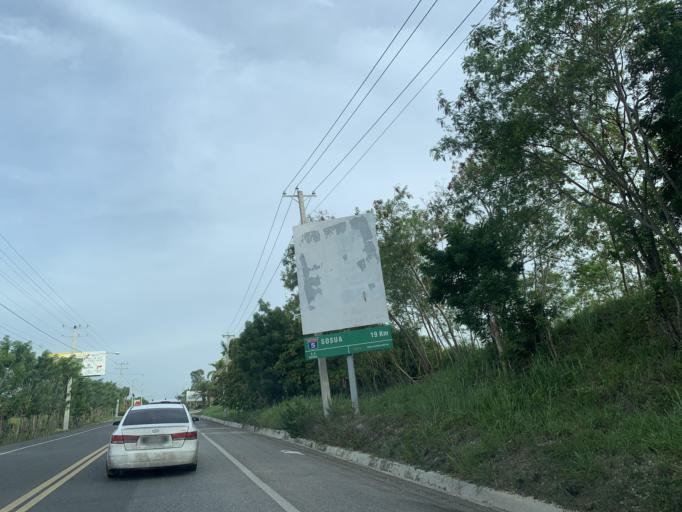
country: DO
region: Puerto Plata
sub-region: Puerto Plata
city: Puerto Plata
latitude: 19.7361
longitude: -70.6302
